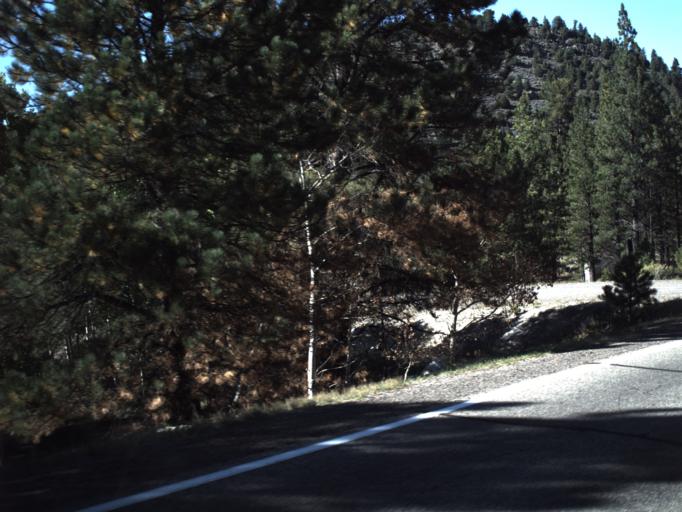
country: US
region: Utah
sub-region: Iron County
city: Parowan
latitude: 37.6954
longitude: -112.6639
